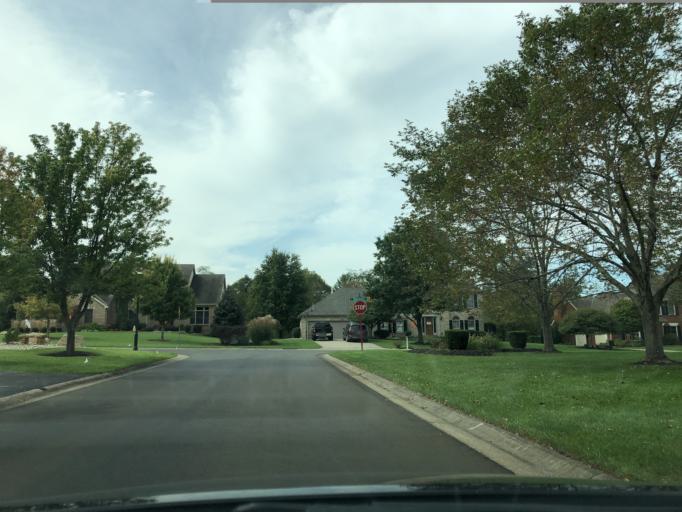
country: US
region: Ohio
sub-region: Hamilton County
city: Loveland
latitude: 39.2444
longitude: -84.2670
